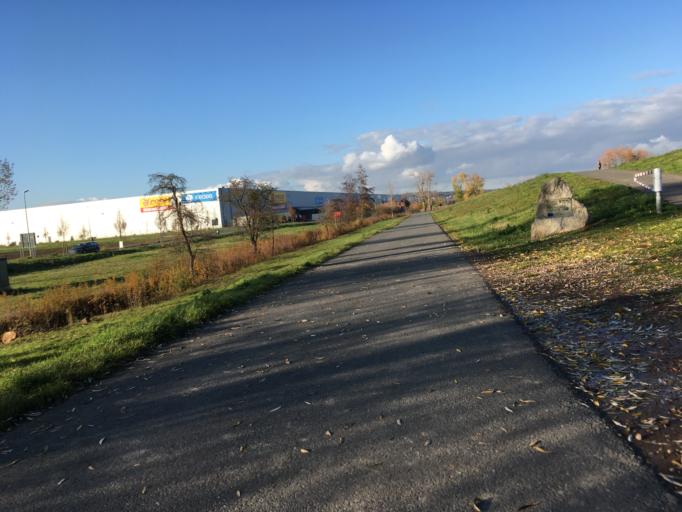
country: DE
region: Rheinland-Pfalz
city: Nackenheim
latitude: 49.9279
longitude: 8.3331
